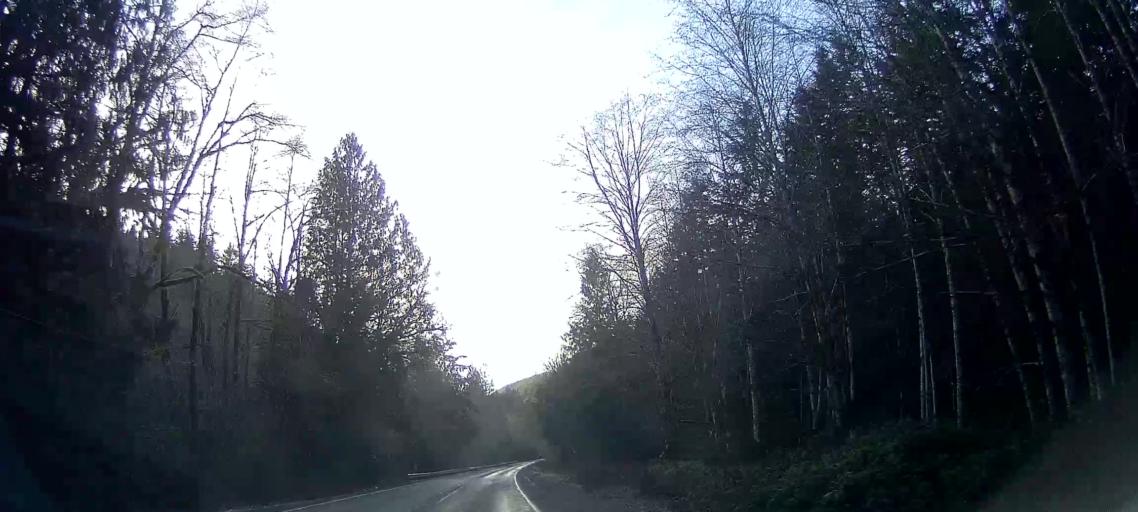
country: US
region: Washington
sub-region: Snohomish County
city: Darrington
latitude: 48.5611
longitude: -121.8266
